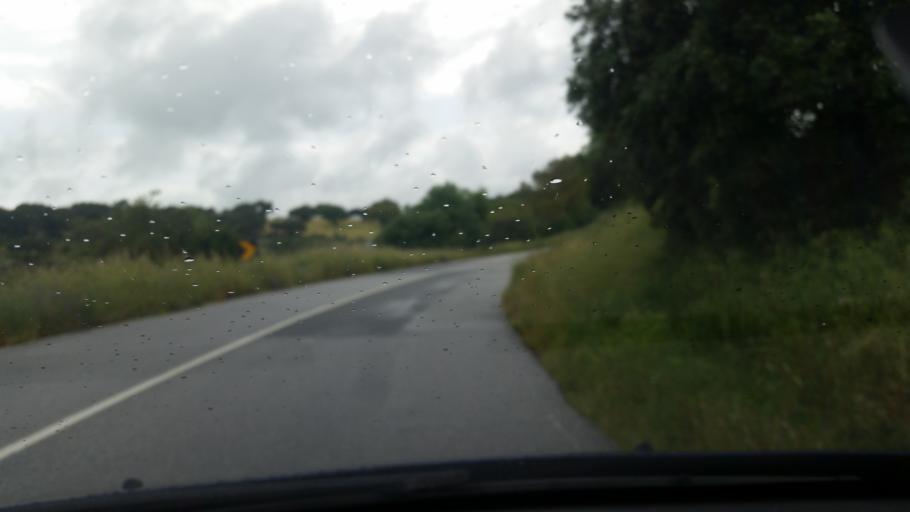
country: PT
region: Evora
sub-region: Arraiolos
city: Arraiolos
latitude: 38.7472
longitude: -7.9924
